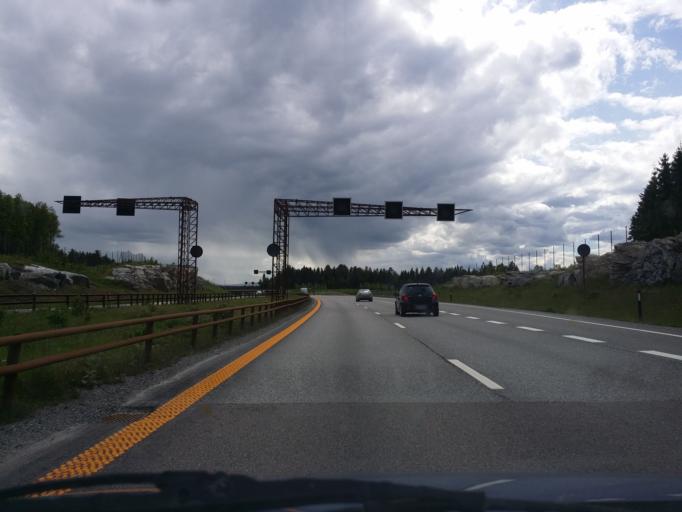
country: NO
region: Akershus
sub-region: Eidsvoll
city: Raholt
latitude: 60.3358
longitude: 11.1943
